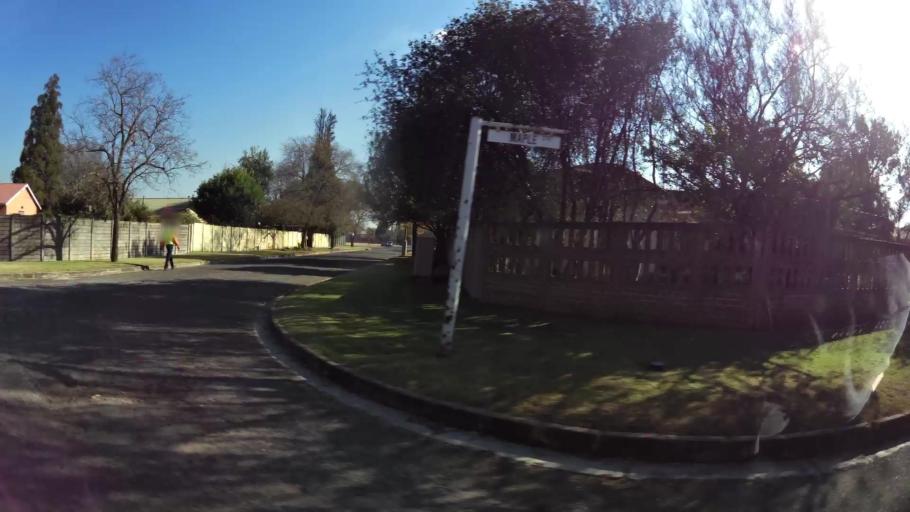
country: ZA
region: Gauteng
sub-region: Ekurhuleni Metropolitan Municipality
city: Benoni
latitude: -26.1568
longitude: 28.3085
